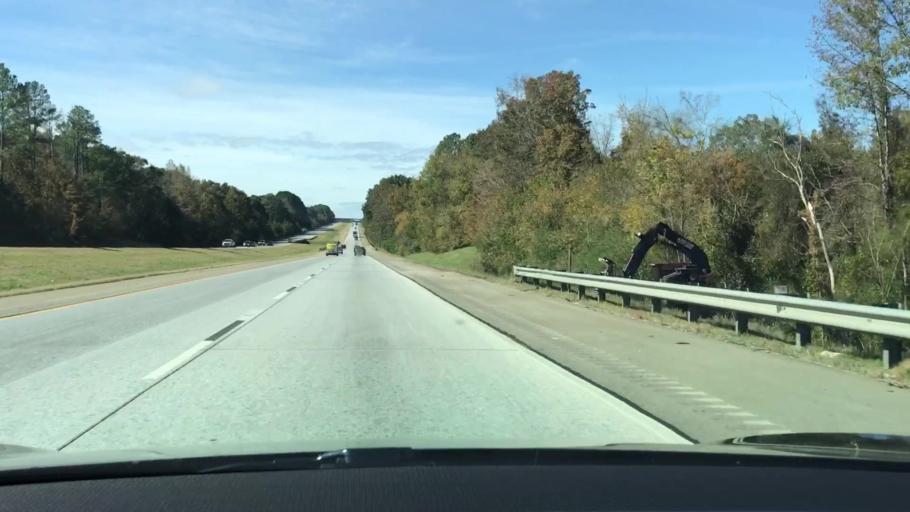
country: US
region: Georgia
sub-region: Greene County
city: Greensboro
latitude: 33.5434
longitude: -83.2201
